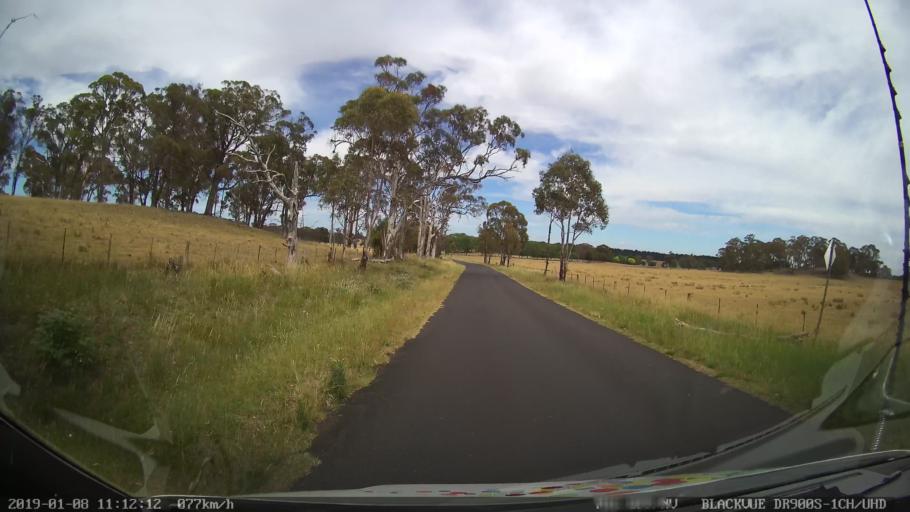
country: AU
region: New South Wales
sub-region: Guyra
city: Guyra
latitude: -30.2275
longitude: 151.6146
